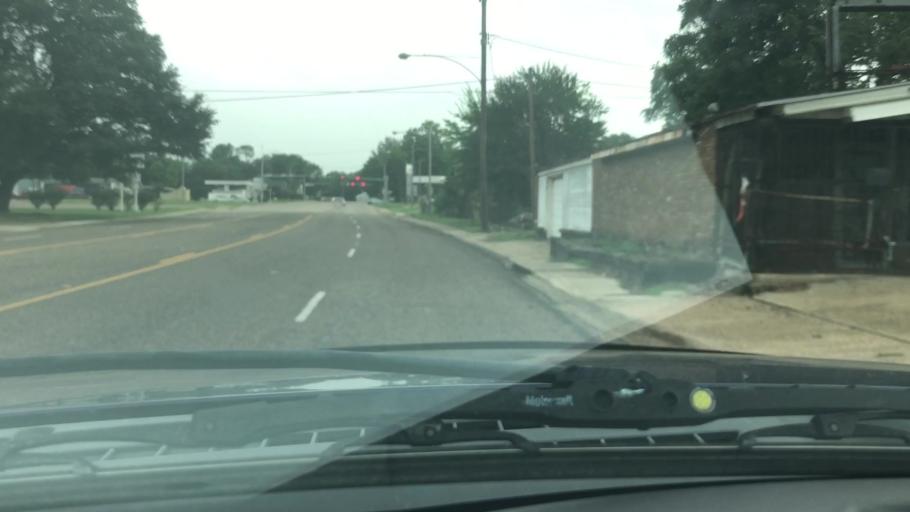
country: US
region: Texas
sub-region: Bowie County
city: Texarkana
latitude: 33.4215
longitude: -94.0609
